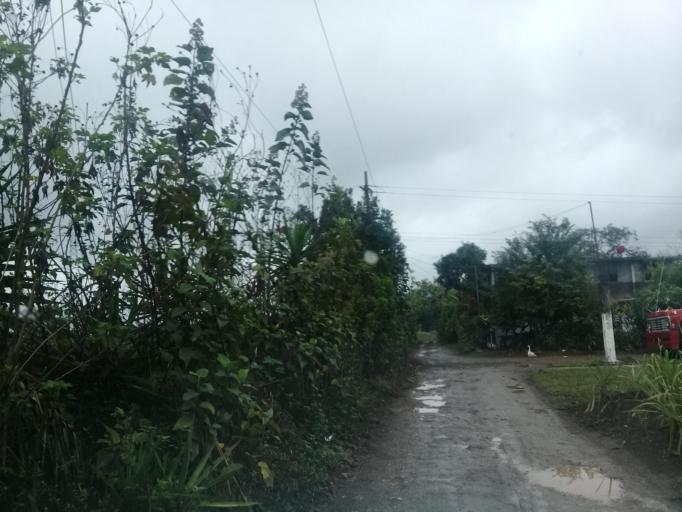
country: MX
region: Veracruz
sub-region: Amatlan de los Reyes
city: Centro de Readaptacion Social
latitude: 18.8232
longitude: -96.9555
